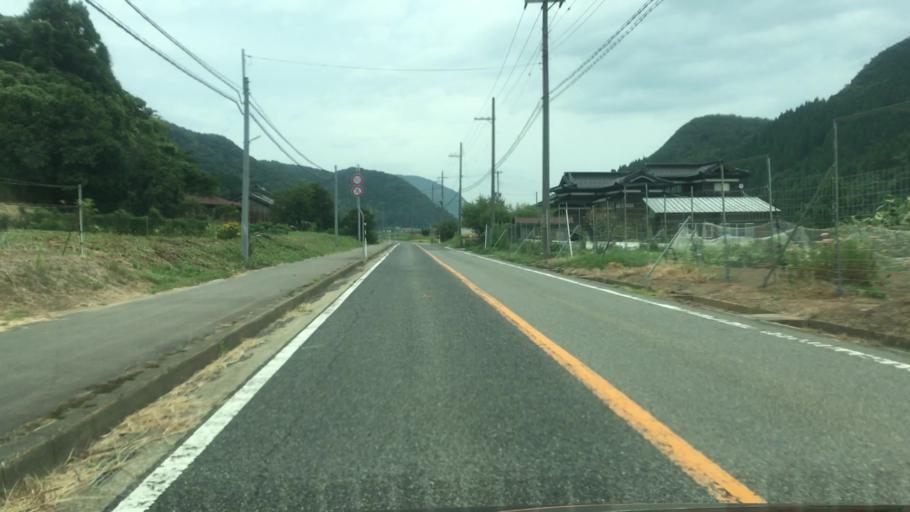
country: JP
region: Hyogo
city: Toyooka
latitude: 35.6308
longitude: 134.6800
